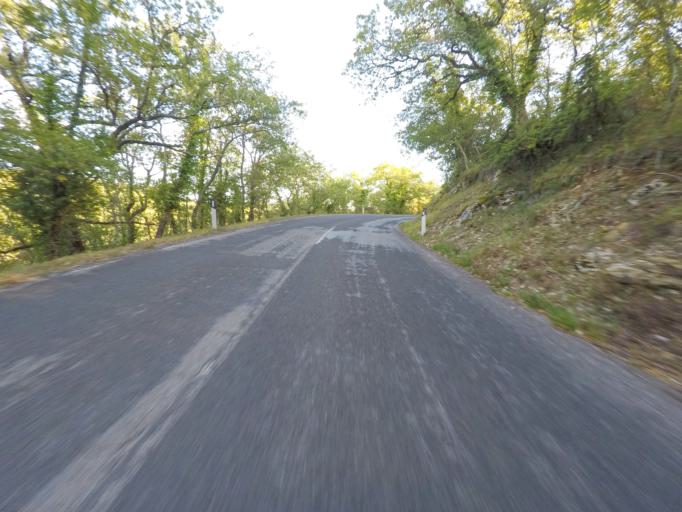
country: IT
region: Tuscany
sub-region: Provincia di Siena
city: Radda in Chianti
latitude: 43.4598
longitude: 11.3865
